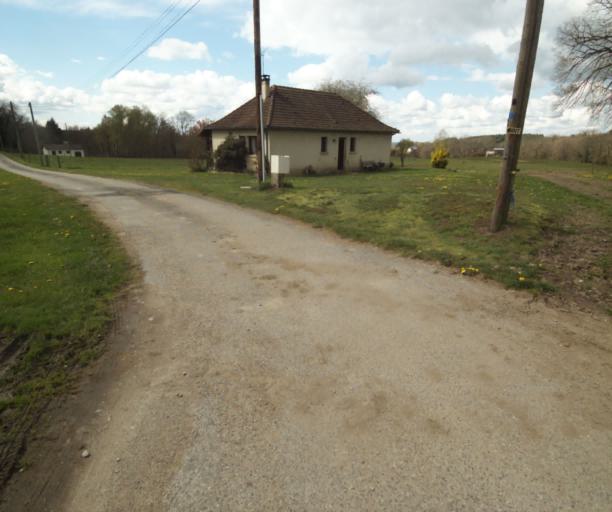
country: FR
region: Limousin
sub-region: Departement de la Correze
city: Correze
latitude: 45.2563
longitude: 1.9019
